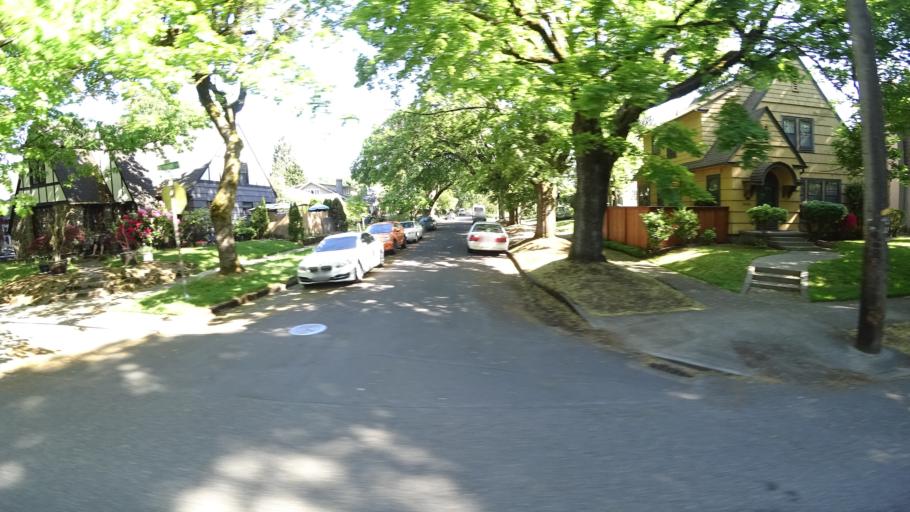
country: US
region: Oregon
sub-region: Multnomah County
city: Portland
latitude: 45.5483
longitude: -122.6451
